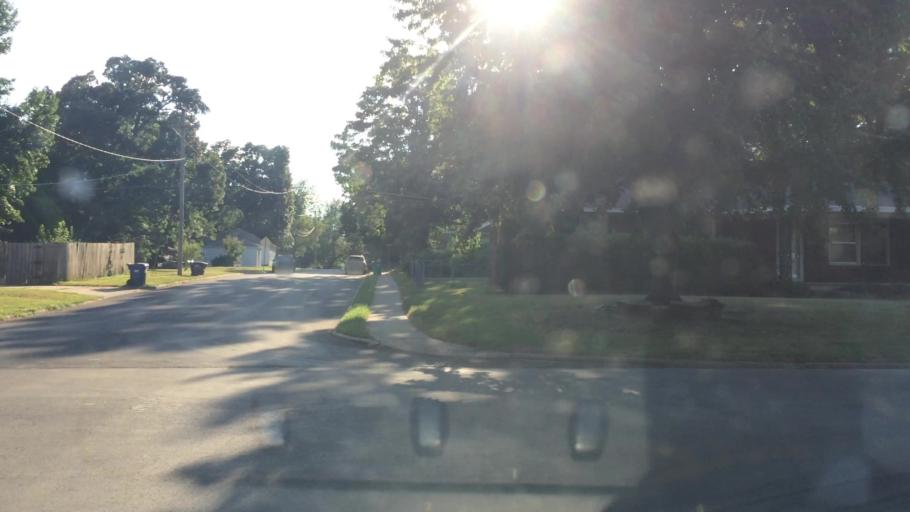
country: US
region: Missouri
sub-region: Greene County
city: Springfield
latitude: 37.2013
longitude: -93.2565
